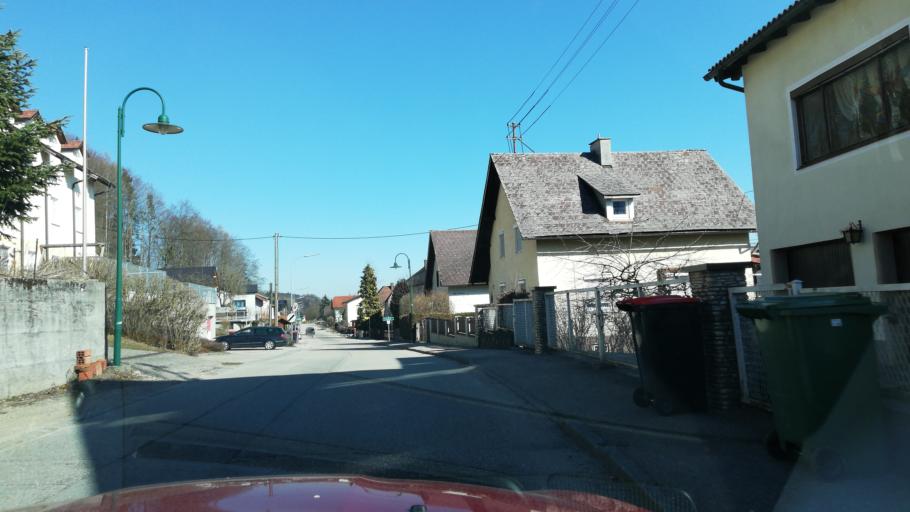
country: AT
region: Upper Austria
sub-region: Politischer Bezirk Vocklabruck
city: Redlham
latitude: 48.0202
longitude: 13.7231
